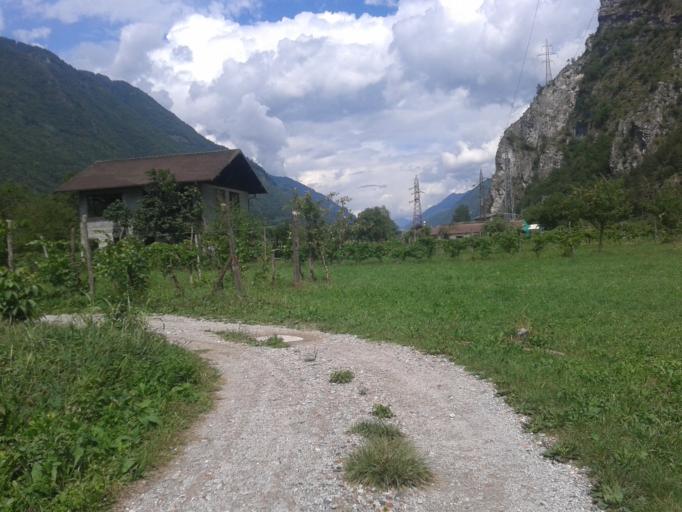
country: IT
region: Trentino-Alto Adige
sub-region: Provincia di Trento
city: Storo
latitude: 45.8564
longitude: 10.5725
